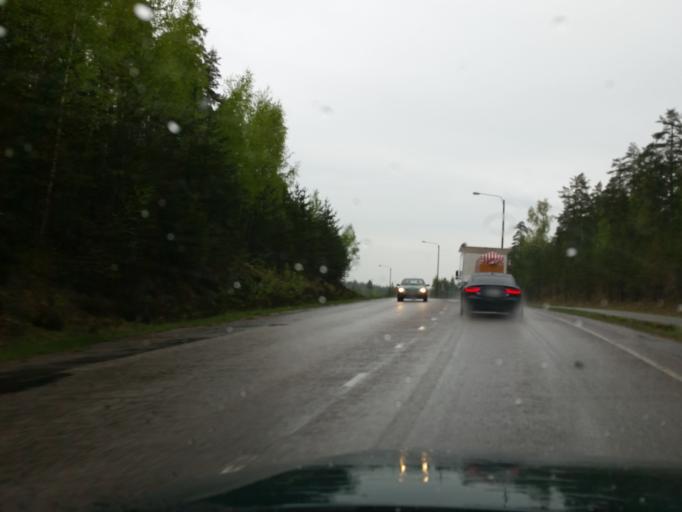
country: FI
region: Uusimaa
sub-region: Helsinki
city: Vihti
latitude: 60.3459
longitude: 24.3211
